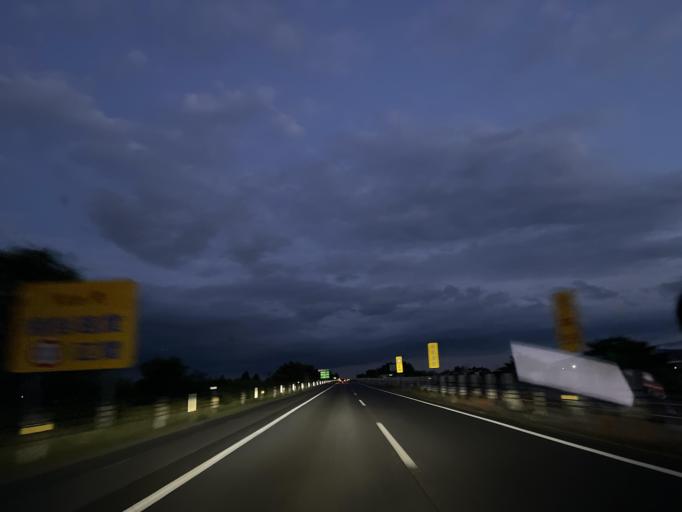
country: JP
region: Iwate
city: Morioka-shi
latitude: 39.6432
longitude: 141.1254
